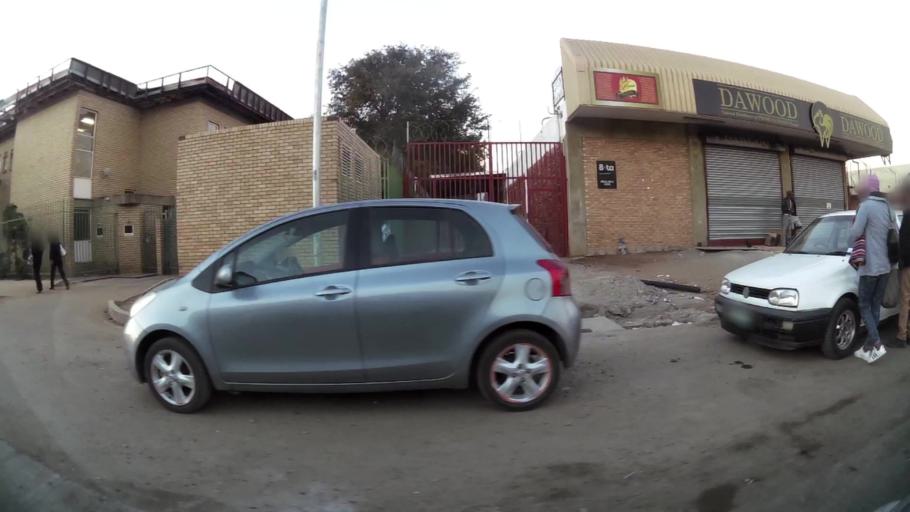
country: ZA
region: North-West
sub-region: Bojanala Platinum District Municipality
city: Rustenburg
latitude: -25.6662
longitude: 27.2369
